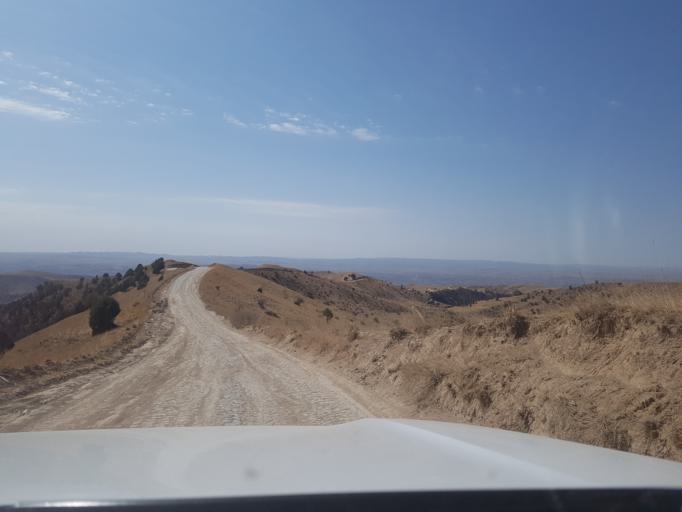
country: TM
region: Ahal
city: Baharly
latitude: 38.2920
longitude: 56.9338
